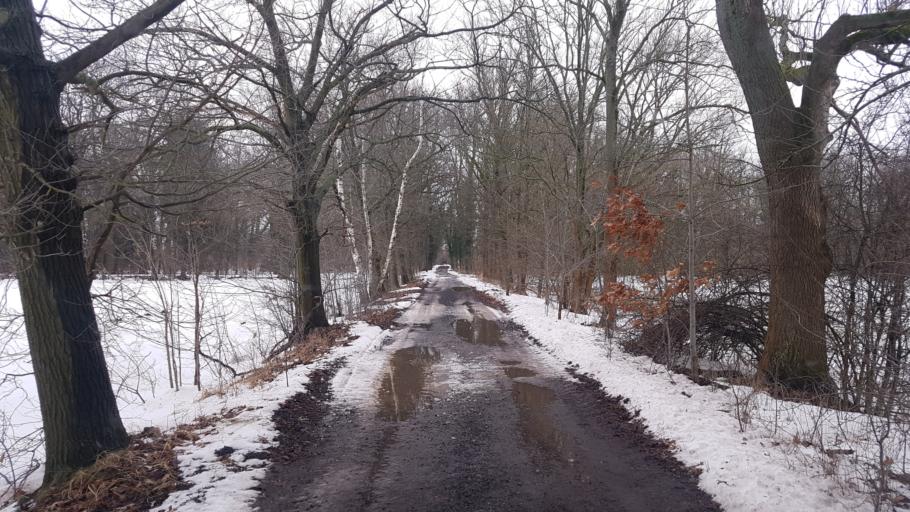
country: DE
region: Brandenburg
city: Bronkow
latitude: 51.6106
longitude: 13.9053
